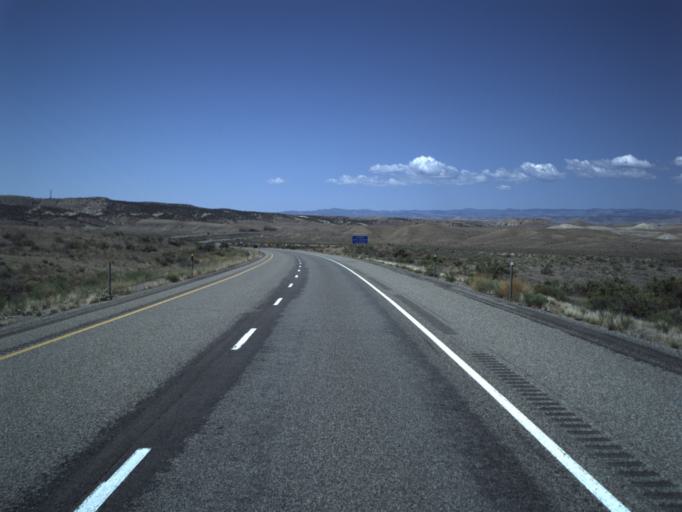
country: US
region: Colorado
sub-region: Mesa County
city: Loma
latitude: 39.1951
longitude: -109.0653
